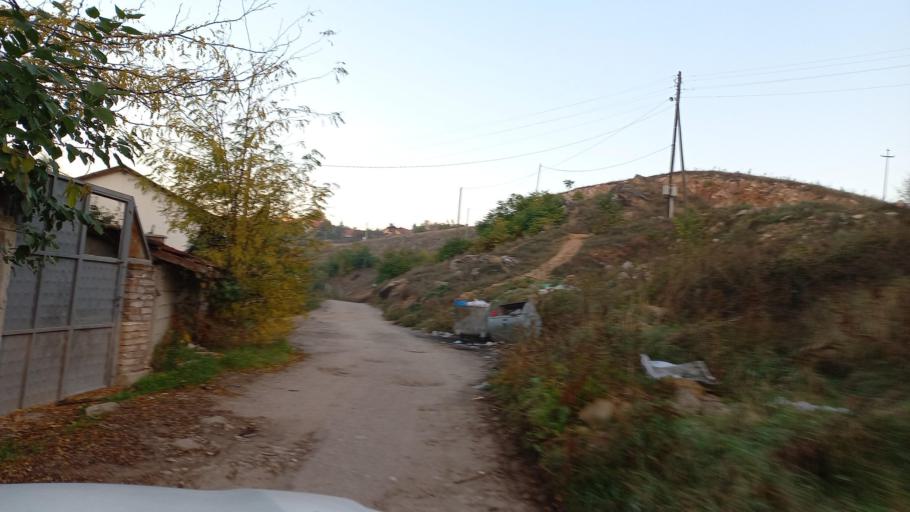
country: MK
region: Kumanovo
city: Kumanovo
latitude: 42.1381
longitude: 21.7282
